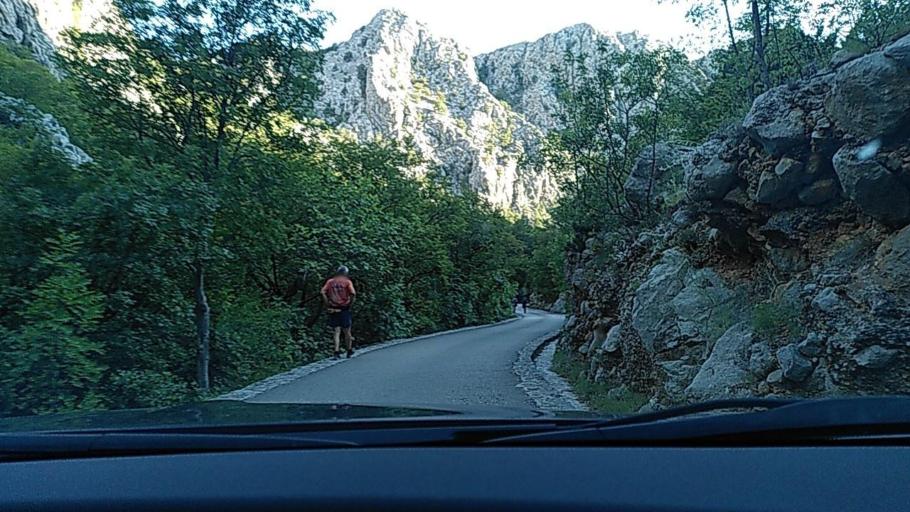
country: HR
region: Zadarska
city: Starigrad
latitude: 44.3021
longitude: 15.4708
